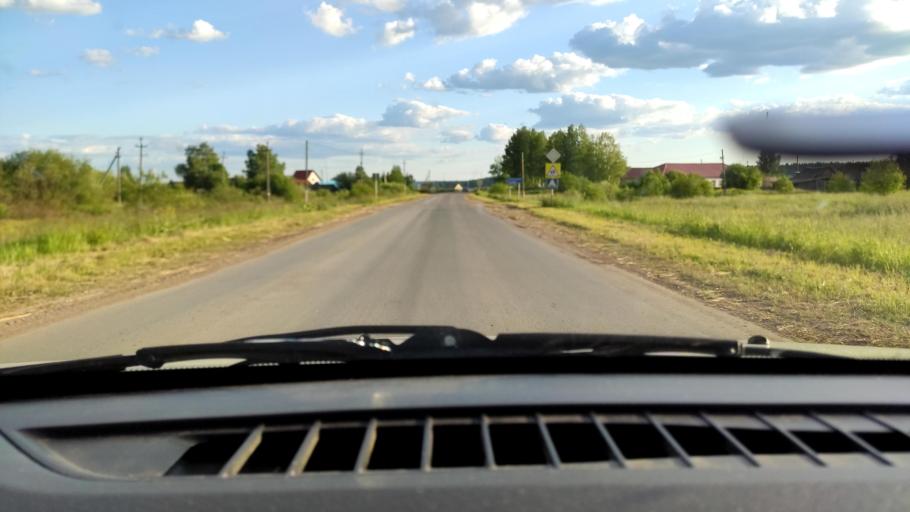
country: RU
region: Perm
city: Uinskoye
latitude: 57.0961
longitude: 56.6423
